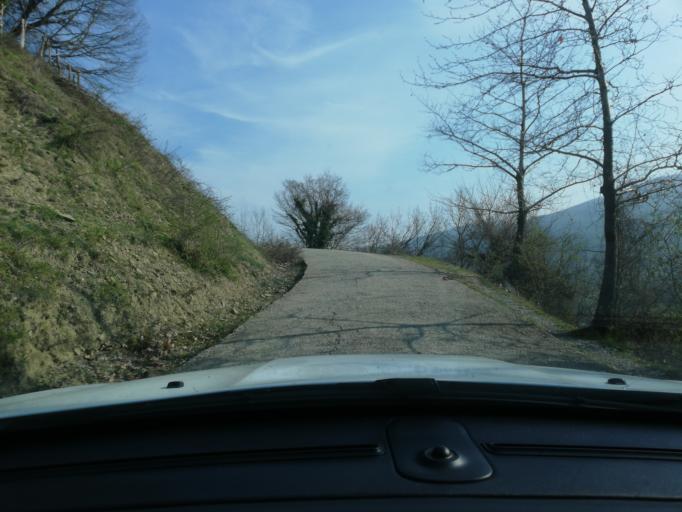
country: TR
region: Karabuk
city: Yenice
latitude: 41.2666
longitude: 32.3600
